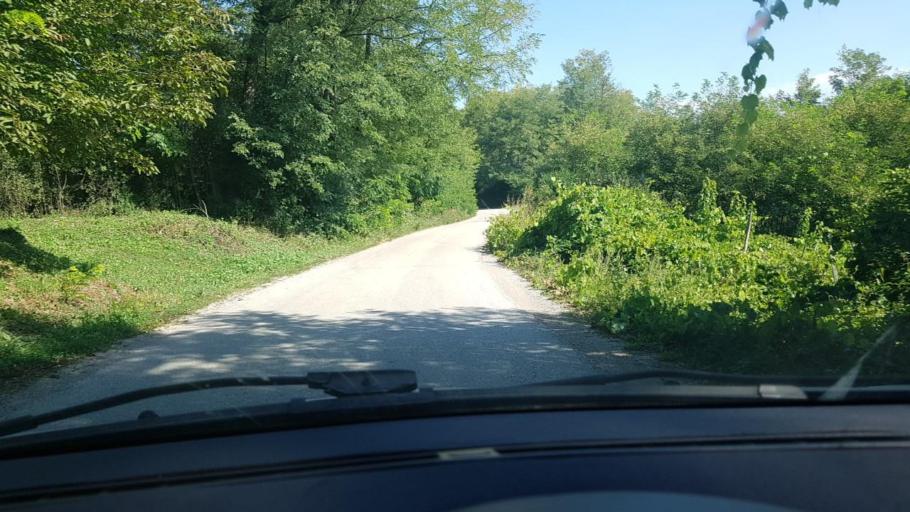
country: HR
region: Karlovacka
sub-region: Grad Karlovac
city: Karlovac
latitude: 45.4774
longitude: 15.4324
